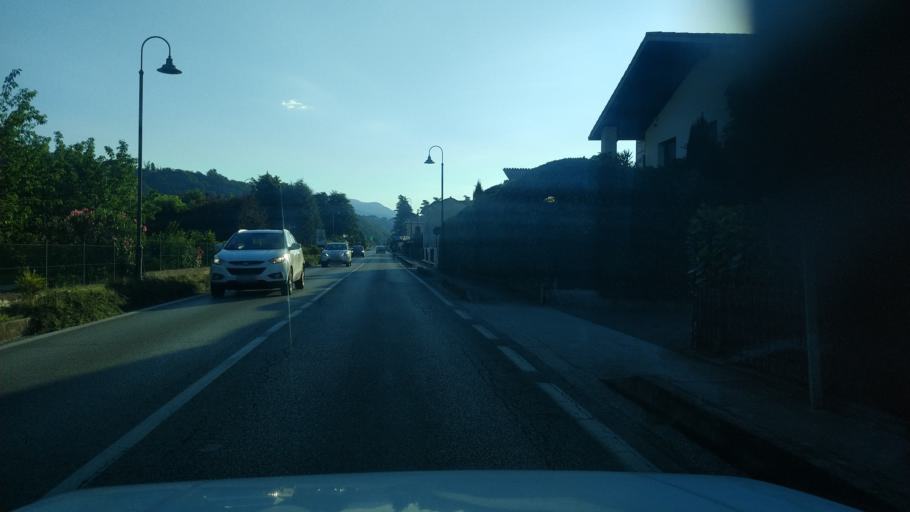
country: IT
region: Veneto
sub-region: Provincia di Vicenza
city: Pianezze
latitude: 45.7349
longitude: 11.6356
